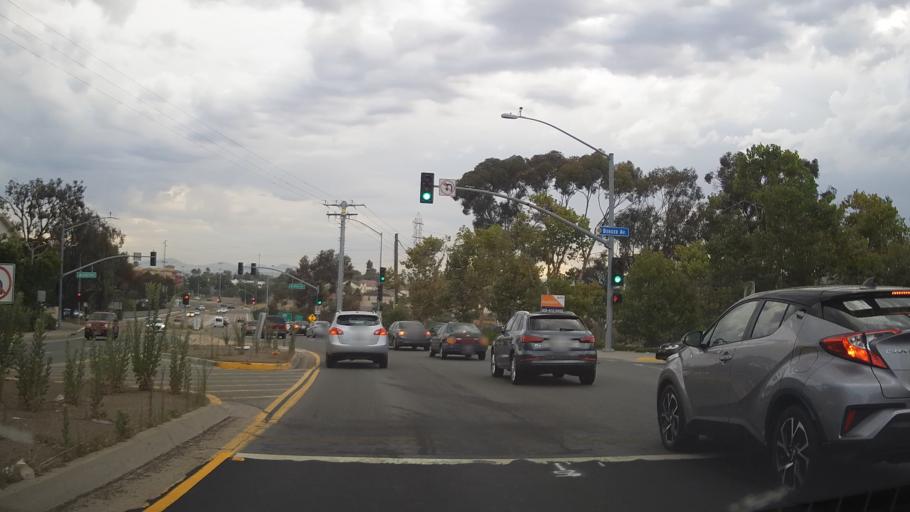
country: US
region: California
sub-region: San Diego County
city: San Diego
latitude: 32.8024
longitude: -117.1522
